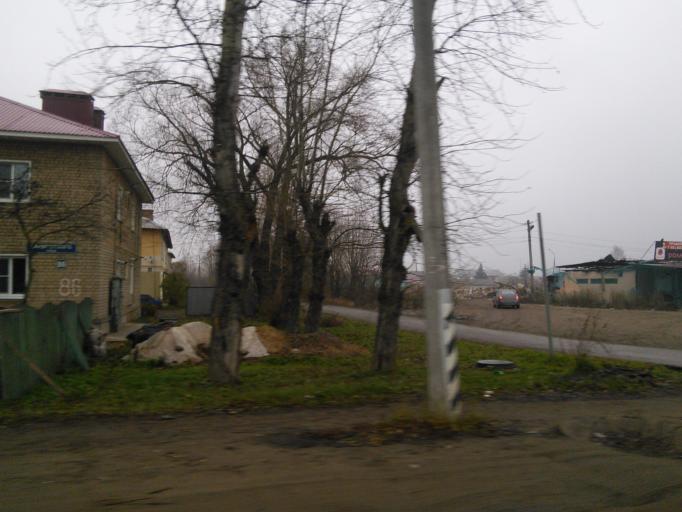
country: RU
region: Jaroslavl
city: Pereslavl'-Zalesskiy
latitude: 56.7227
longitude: 38.8340
